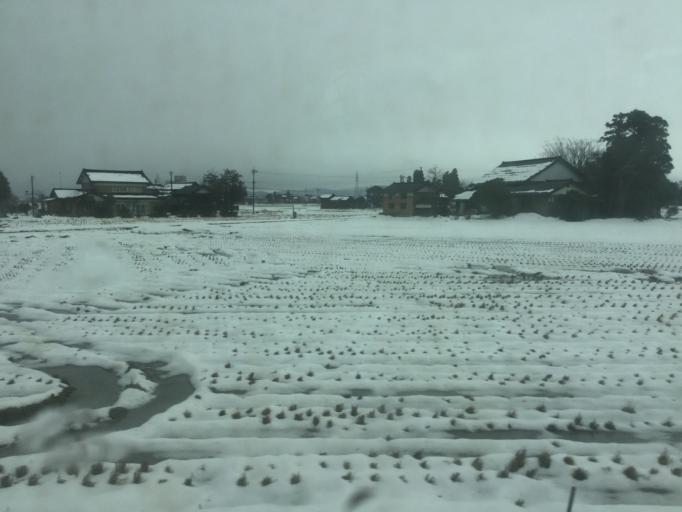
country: JP
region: Toyama
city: Nanto-shi
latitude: 36.6225
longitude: 136.9457
